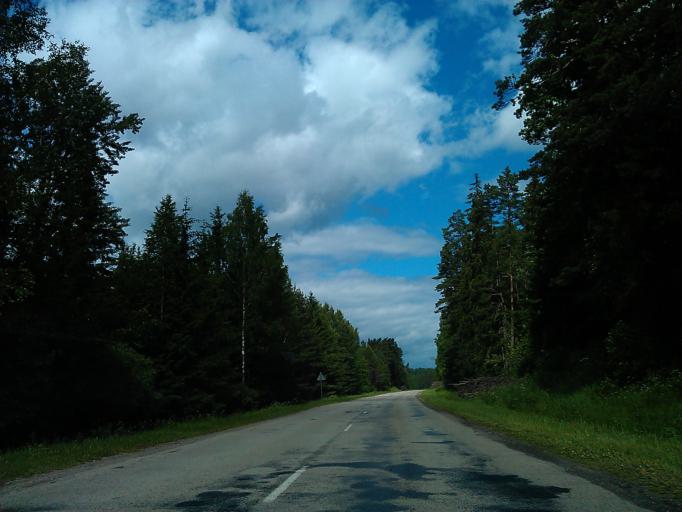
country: LV
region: Talsu Rajons
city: Sabile
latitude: 57.0723
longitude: 22.5342
